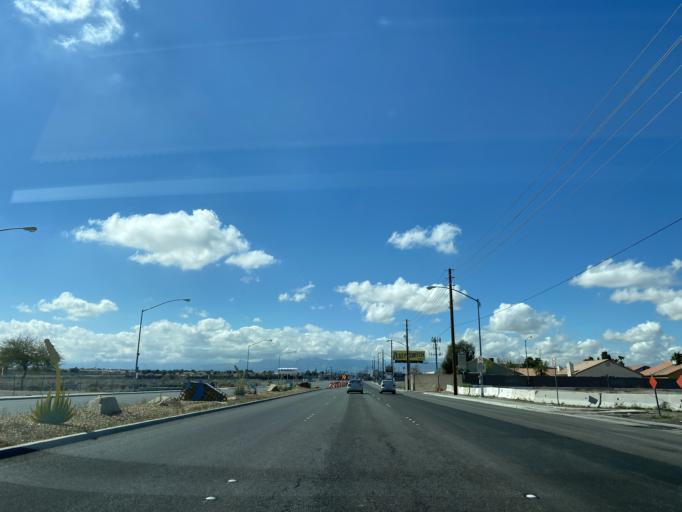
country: US
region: Nevada
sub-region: Clark County
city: North Las Vegas
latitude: 36.2397
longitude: -115.1287
